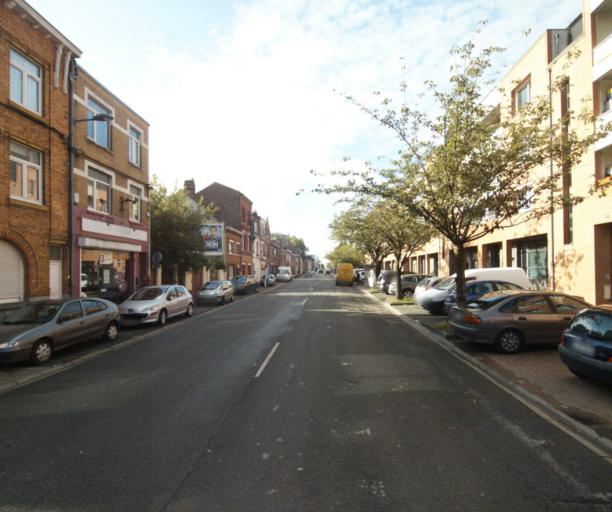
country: FR
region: Nord-Pas-de-Calais
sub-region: Departement du Nord
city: Wattignies
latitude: 50.6098
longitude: 3.0450
